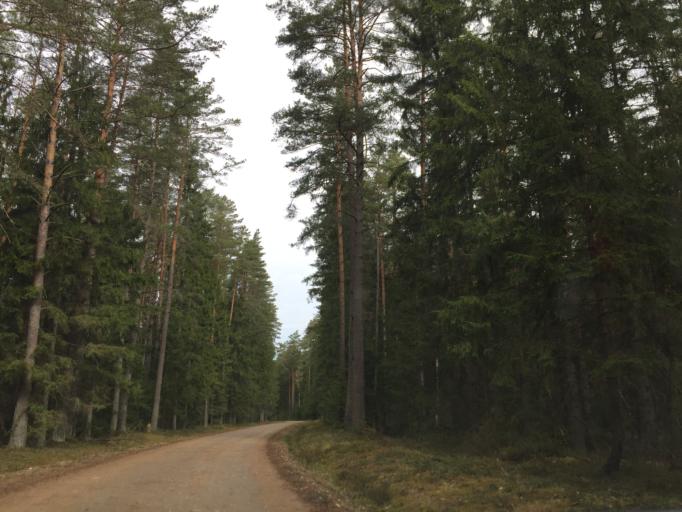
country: LV
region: Saulkrastu
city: Saulkrasti
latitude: 57.5029
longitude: 24.4236
